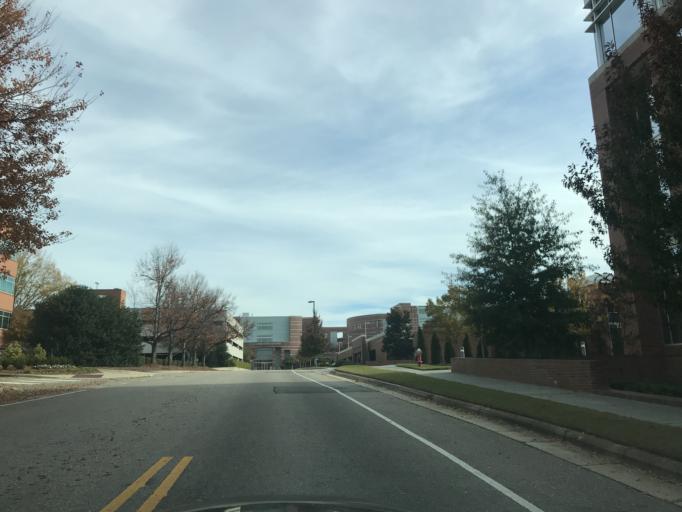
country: US
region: North Carolina
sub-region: Wake County
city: West Raleigh
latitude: 35.7734
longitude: -78.6766
